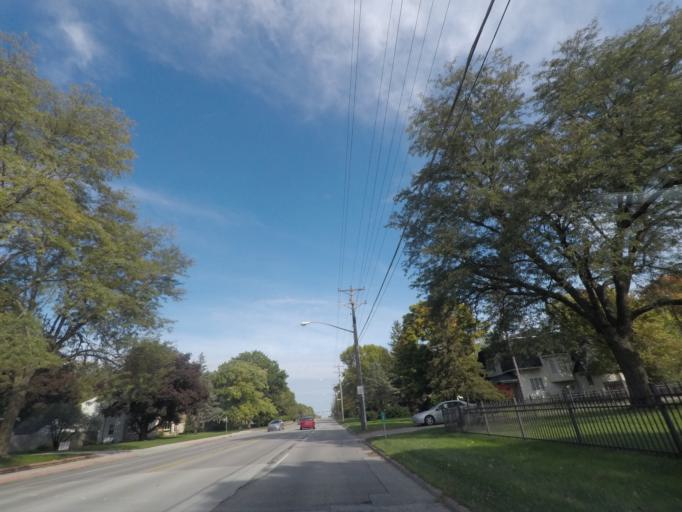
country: US
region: Iowa
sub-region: Story County
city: Ames
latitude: 42.0385
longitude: -93.6204
